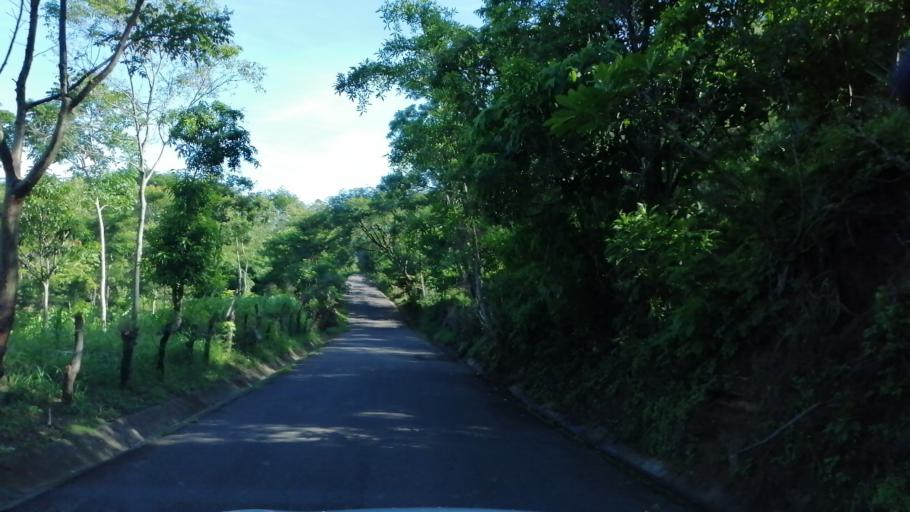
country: SV
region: Morazan
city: Corinto
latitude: 13.8032
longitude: -88.0039
